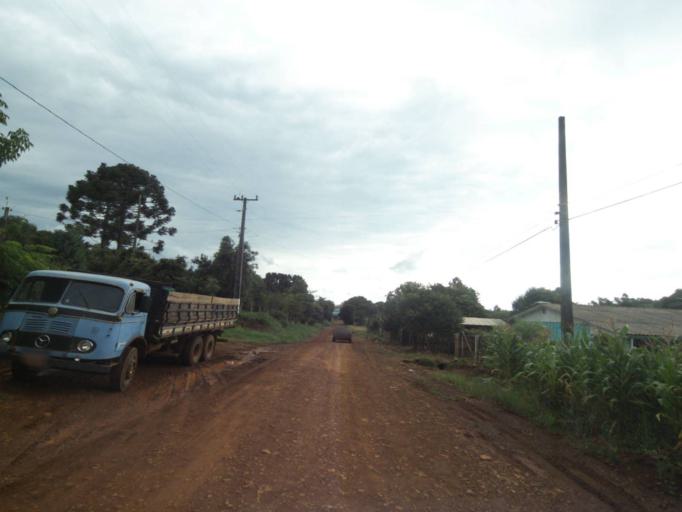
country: BR
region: Parana
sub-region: Pitanga
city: Pitanga
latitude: -24.8972
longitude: -51.9620
